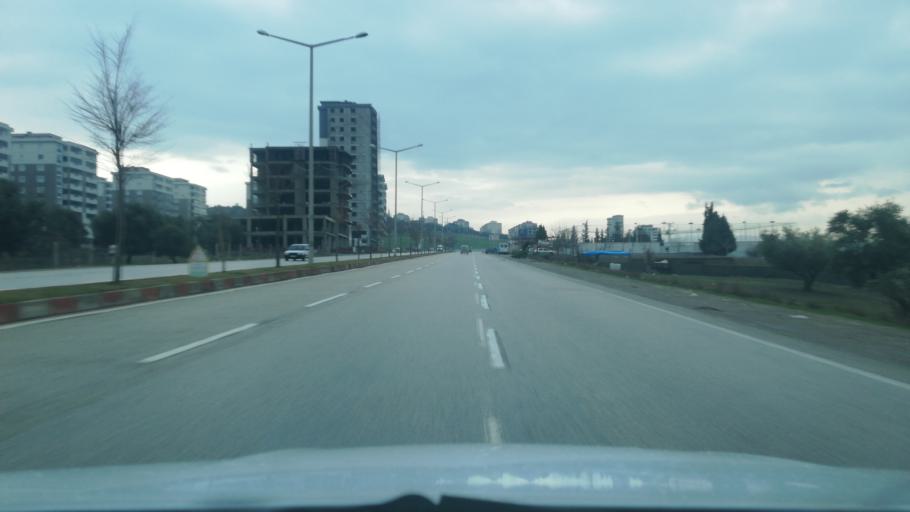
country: TR
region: Kahramanmaras
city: Kahramanmaras
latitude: 37.5822
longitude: 36.9873
